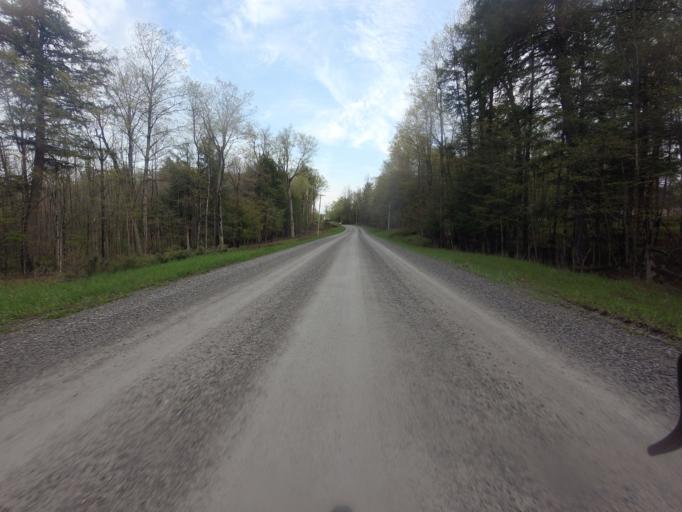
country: CA
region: Ontario
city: Carleton Place
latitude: 45.1966
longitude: -76.3271
